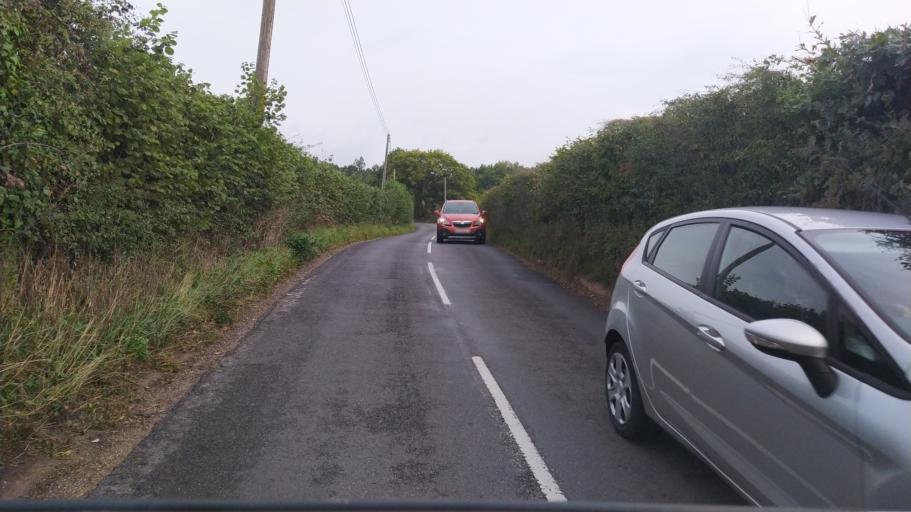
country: GB
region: England
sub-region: Hampshire
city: Romsey
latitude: 51.0257
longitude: -1.5390
